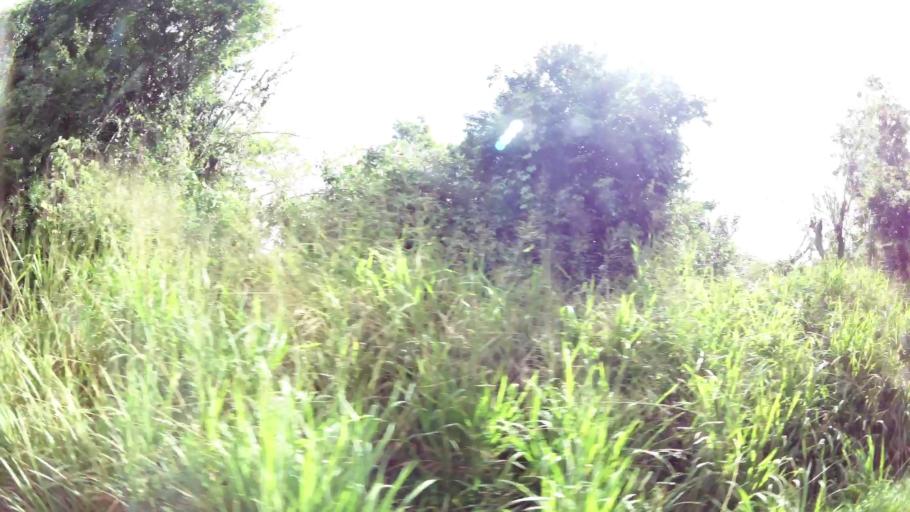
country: MQ
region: Martinique
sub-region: Martinique
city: Sainte-Luce
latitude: 14.4881
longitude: -60.9908
